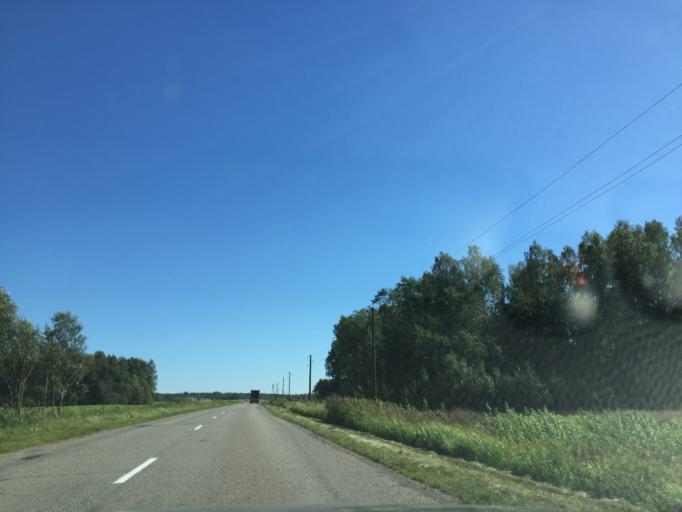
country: LV
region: Akniste
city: Akniste
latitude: 56.1098
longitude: 25.8496
